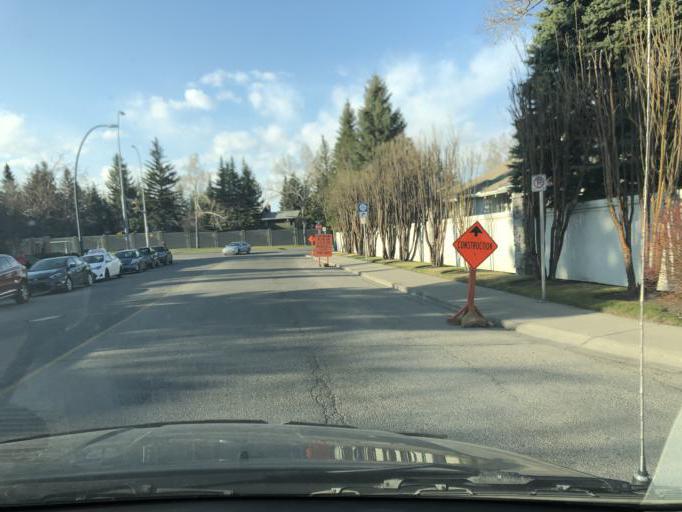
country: CA
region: Alberta
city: Calgary
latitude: 50.9716
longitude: -114.1063
